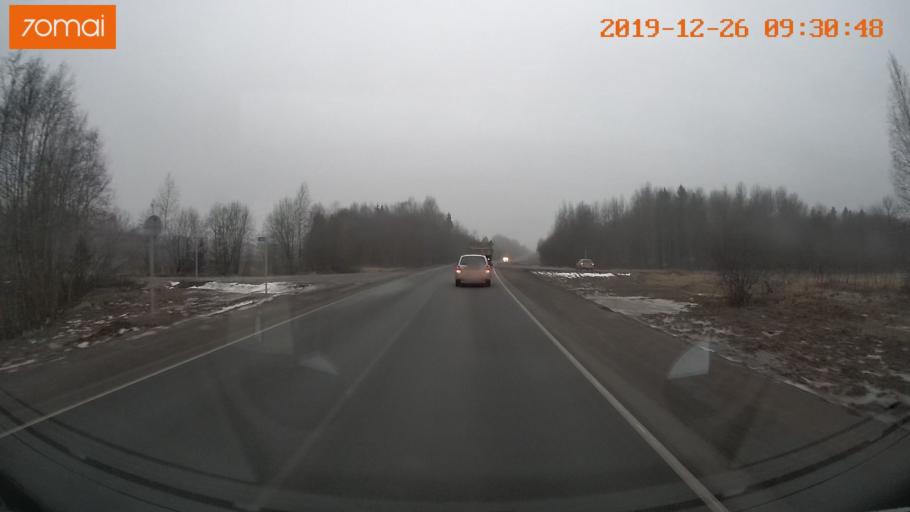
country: RU
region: Vologda
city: Gryazovets
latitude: 59.0635
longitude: 40.1356
